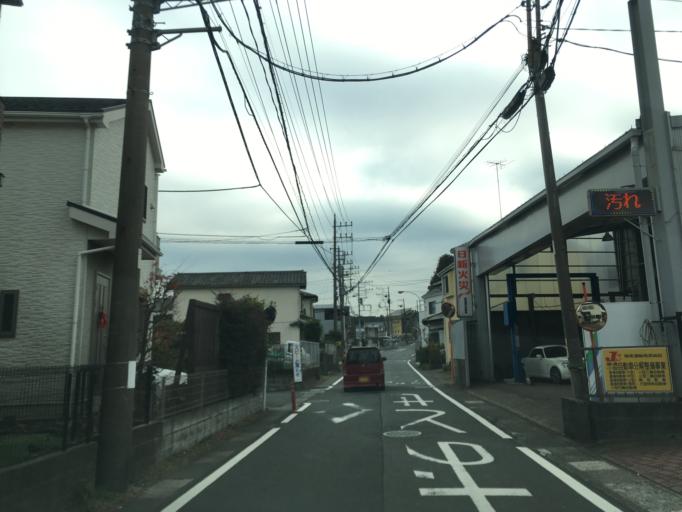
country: JP
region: Kanagawa
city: Minami-rinkan
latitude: 35.5106
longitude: 139.4638
